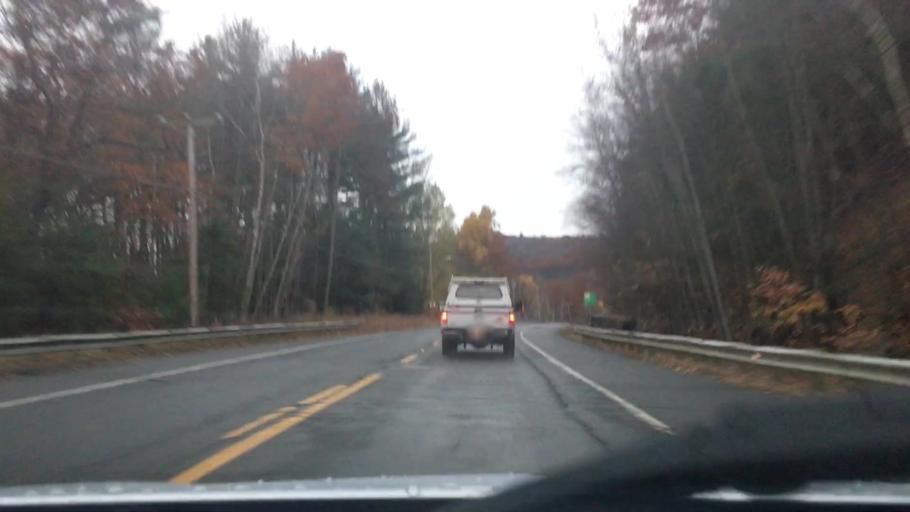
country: US
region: Massachusetts
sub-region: Hampden County
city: Westfield
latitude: 42.1704
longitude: -72.8320
